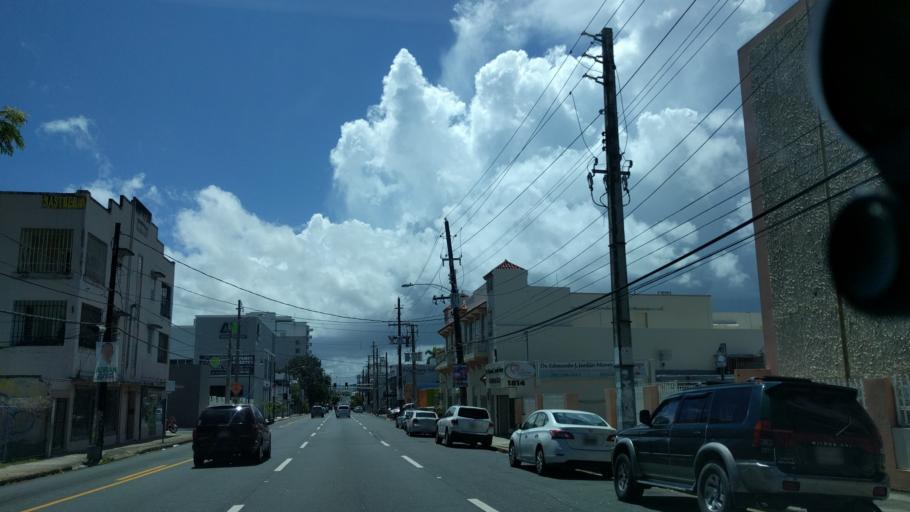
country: PR
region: San Juan
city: San Juan
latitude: 18.4400
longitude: -66.0624
